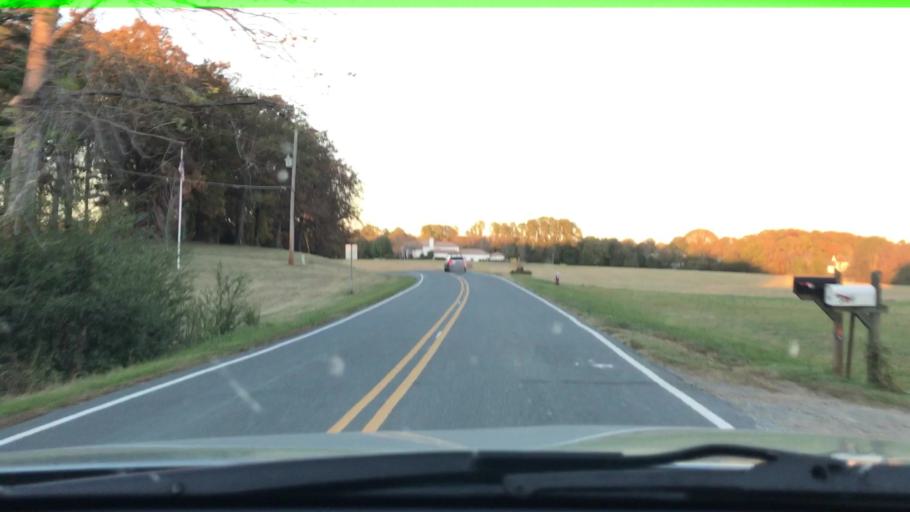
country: US
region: North Carolina
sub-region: Union County
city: Wesley Chapel
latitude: 34.9921
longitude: -80.7146
